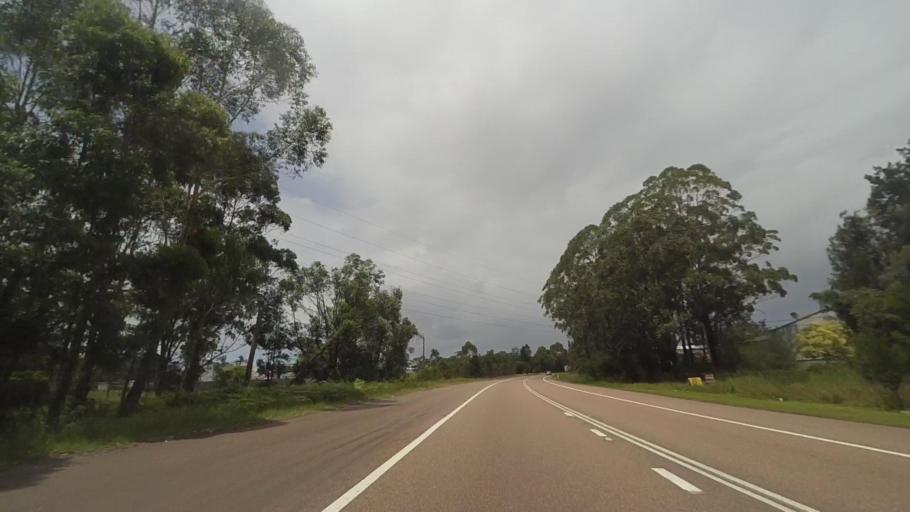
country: AU
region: New South Wales
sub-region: Wyong Shire
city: Chittaway Bay
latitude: -33.3303
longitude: 151.4054
